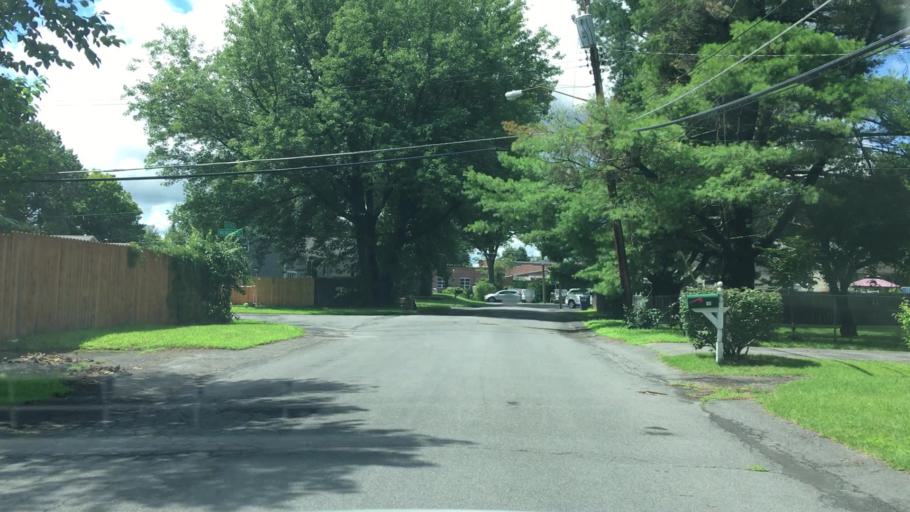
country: US
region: New York
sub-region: Schenectady County
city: Niskayuna
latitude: 42.7451
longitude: -73.8592
